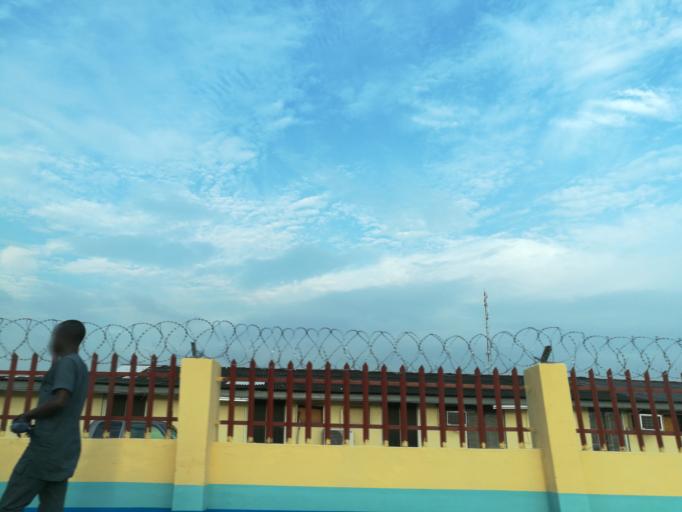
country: NG
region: Lagos
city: Ikeja
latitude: 6.5881
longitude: 3.3339
